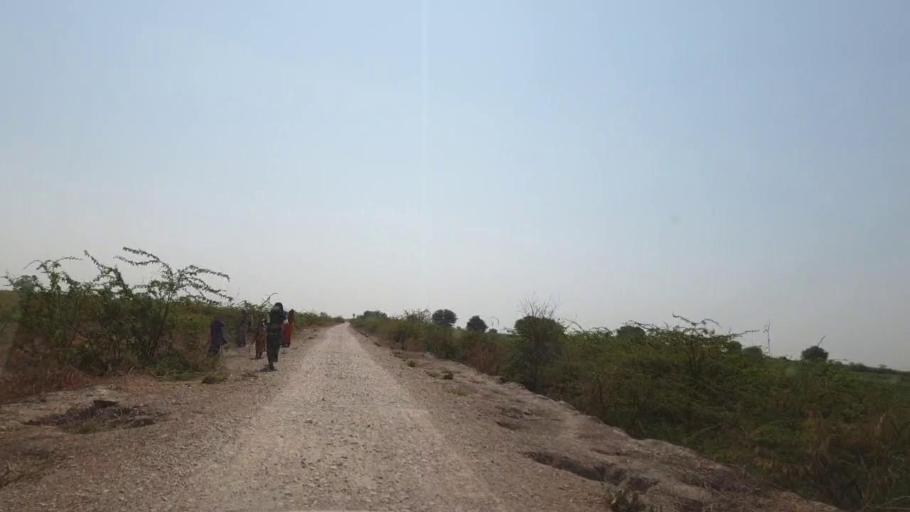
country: PK
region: Sindh
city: Kunri
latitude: 25.0960
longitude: 69.4742
